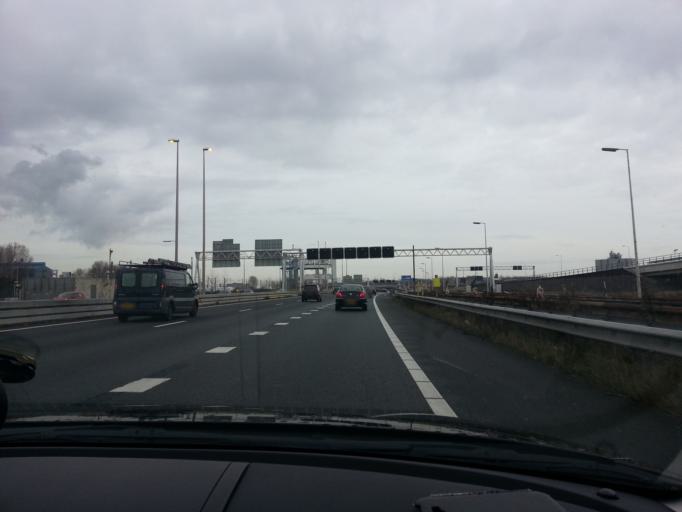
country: NL
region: South Holland
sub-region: Gemeente Spijkenisse
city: Spijkenisse
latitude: 51.8695
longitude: 4.3166
